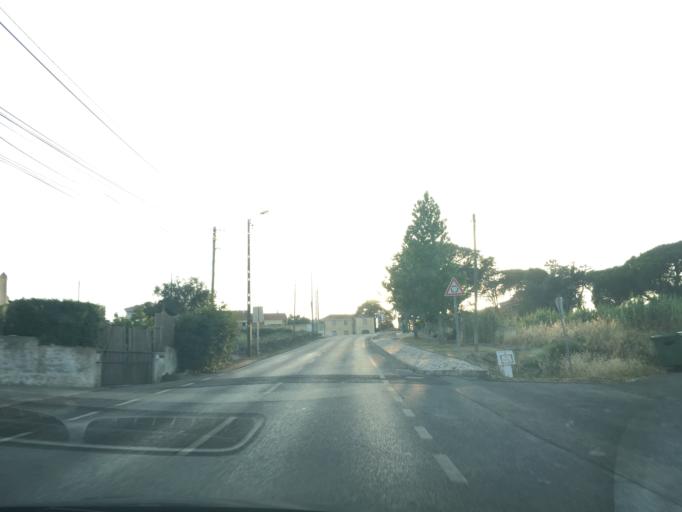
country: PT
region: Lisbon
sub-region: Sintra
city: Sintra
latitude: 38.8173
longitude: -9.4047
